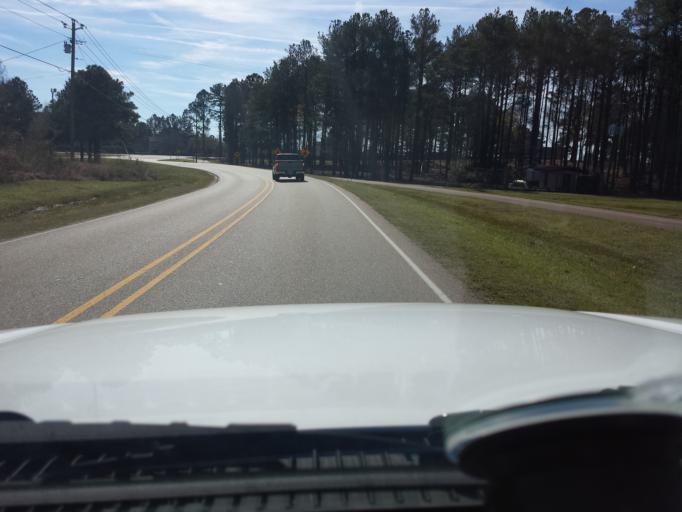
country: US
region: Mississippi
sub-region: Madison County
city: Madison
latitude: 32.4081
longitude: -90.0089
